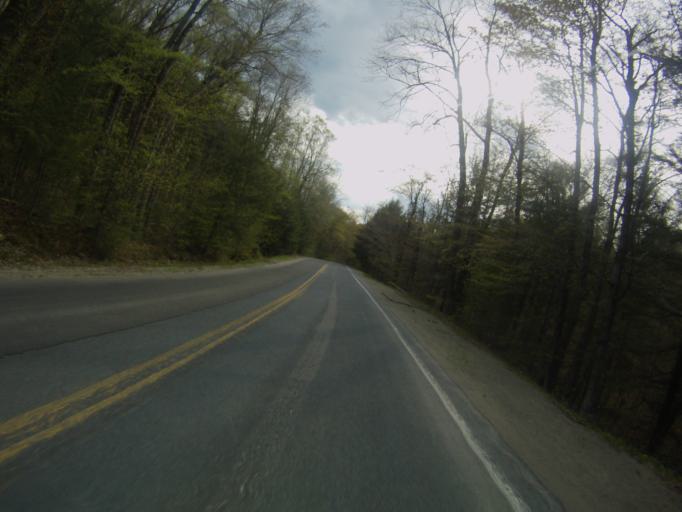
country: US
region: New York
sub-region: Warren County
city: Warrensburg
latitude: 43.8255
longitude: -73.9166
